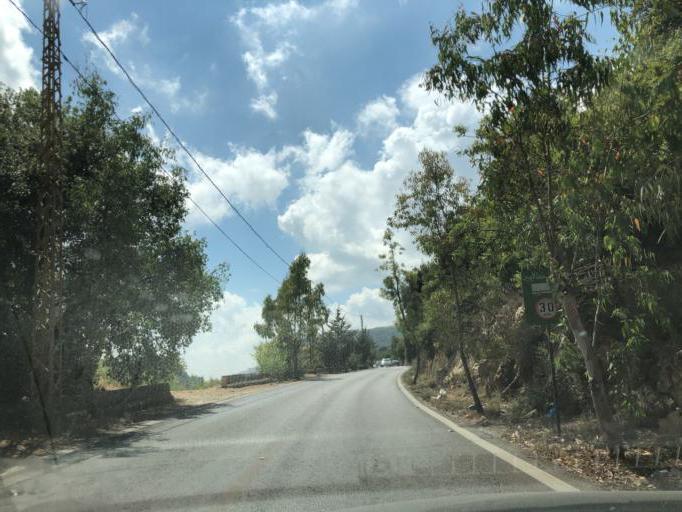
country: LB
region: Mont-Liban
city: Beit ed Dine
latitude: 33.7004
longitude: 35.5941
